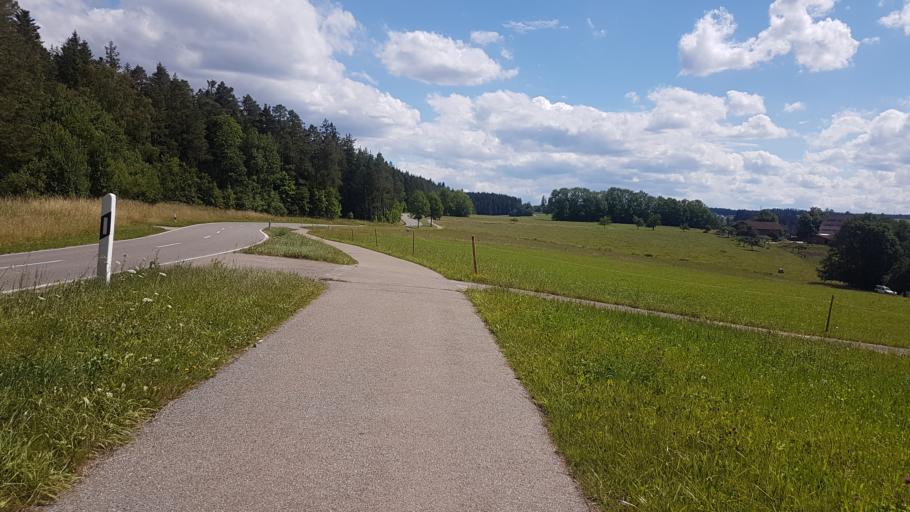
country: DE
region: Baden-Wuerttemberg
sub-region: Freiburg Region
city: Hardt
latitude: 48.2038
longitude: 8.4131
